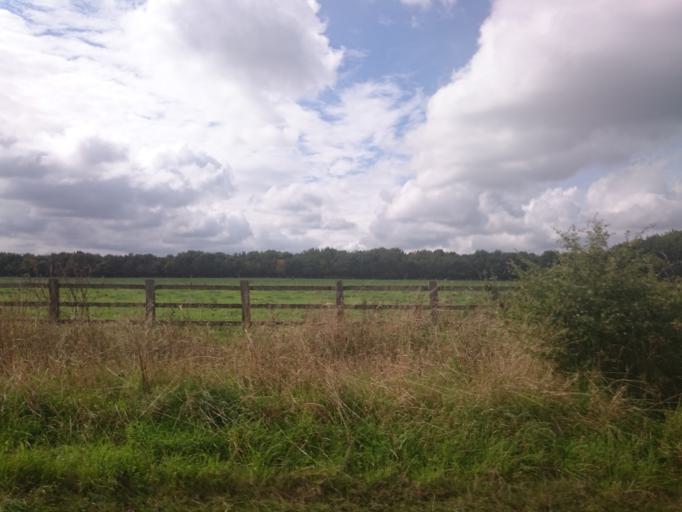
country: GB
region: England
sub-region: Gloucestershire
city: Coates
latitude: 51.7798
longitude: -2.0350
